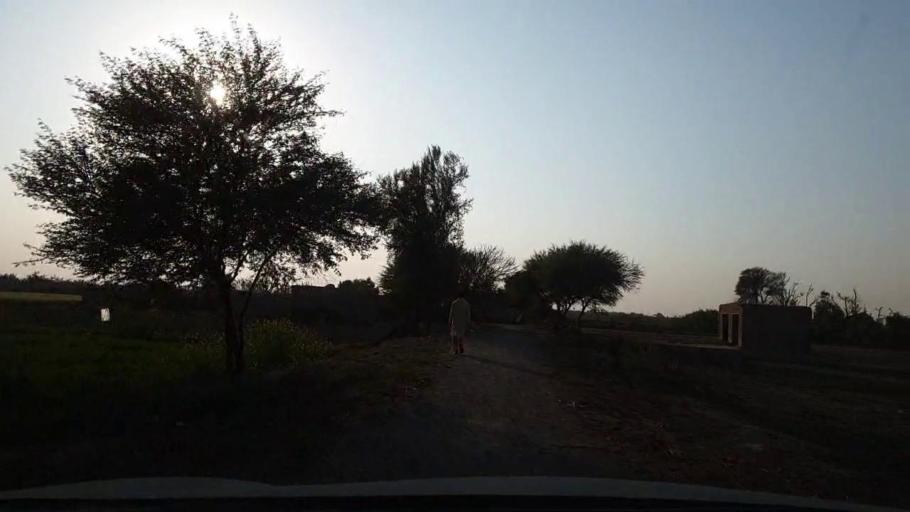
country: PK
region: Sindh
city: Tando Allahyar
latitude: 25.5644
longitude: 68.7915
